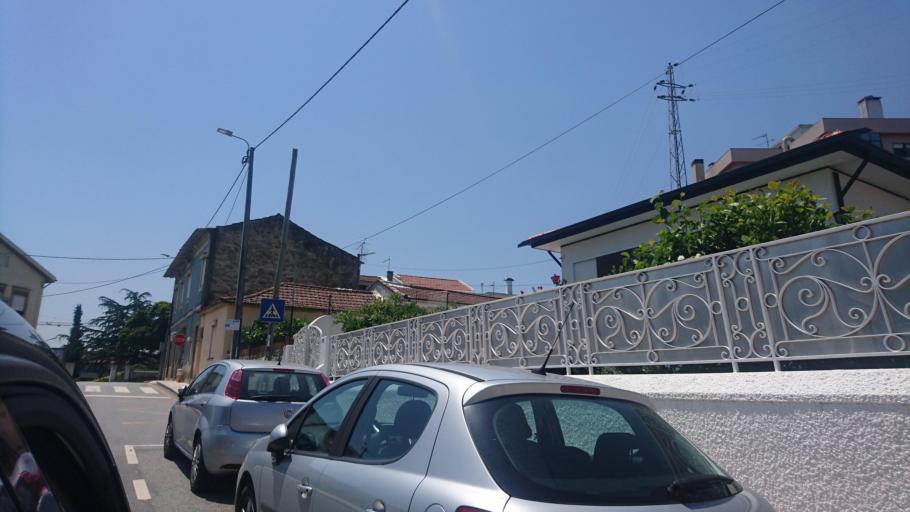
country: PT
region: Porto
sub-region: Gondomar
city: Rio Tinto
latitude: 41.1611
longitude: -8.5494
